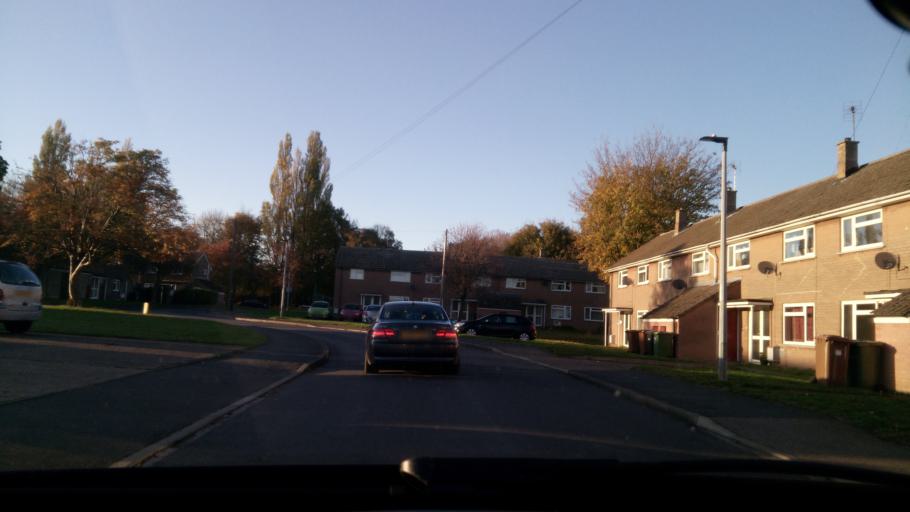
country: GB
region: England
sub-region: Peterborough
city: Wittering
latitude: 52.6090
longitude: -0.4380
